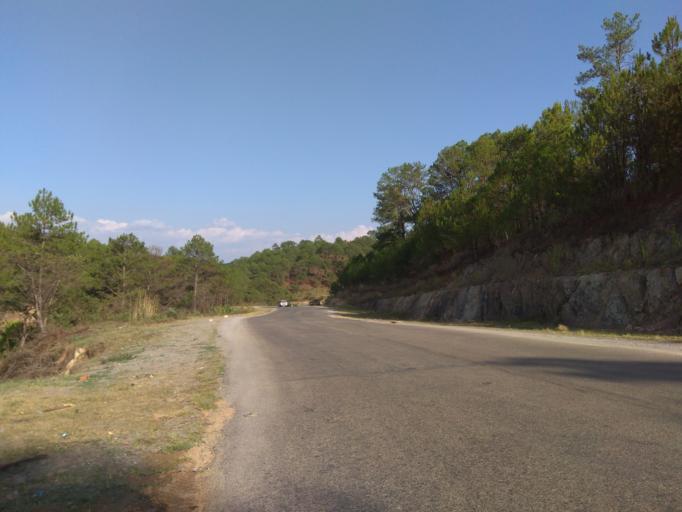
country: MM
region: Shan
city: Taunggyi
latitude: 20.6511
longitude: 96.5934
